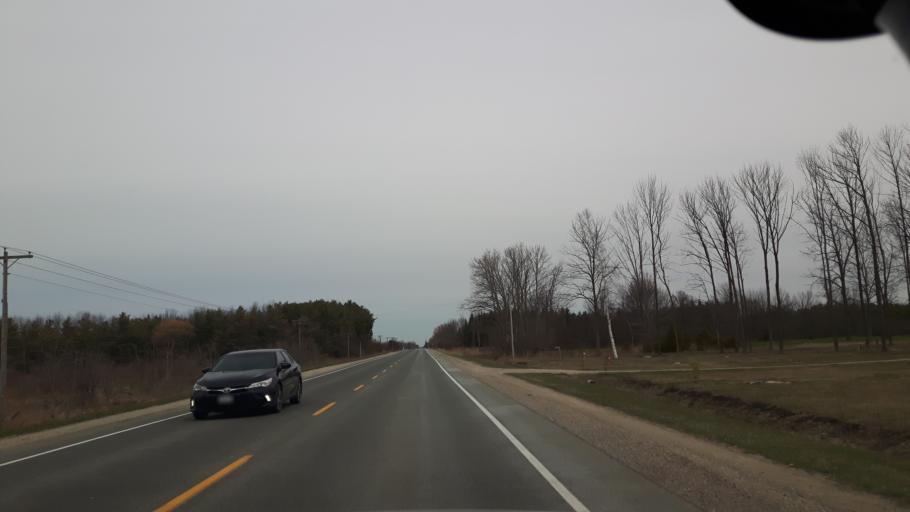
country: CA
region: Ontario
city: Goderich
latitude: 43.6807
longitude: -81.7056
